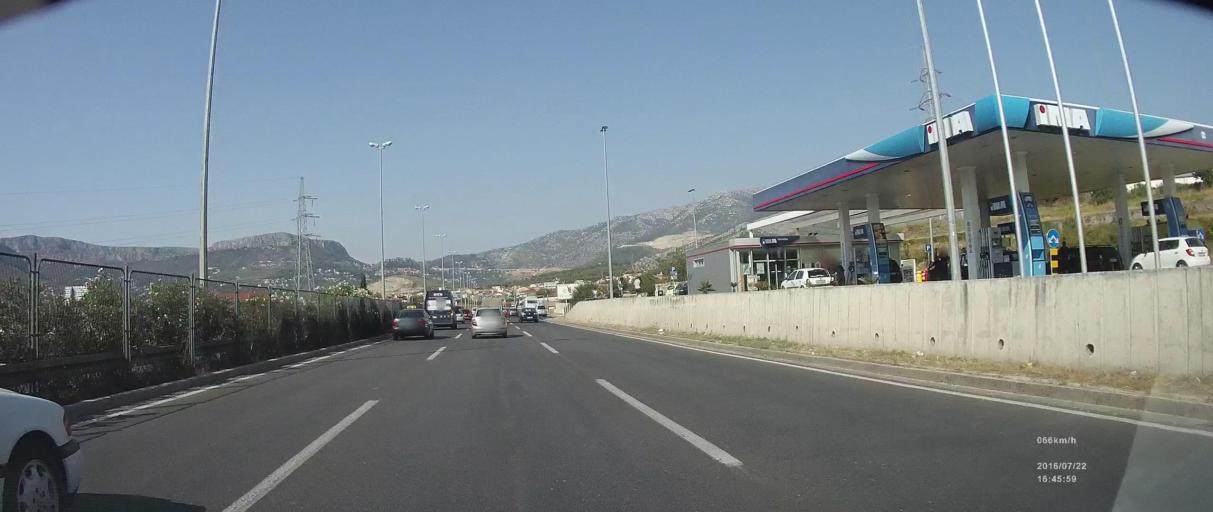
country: HR
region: Splitsko-Dalmatinska
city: Solin
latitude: 43.5231
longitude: 16.4865
